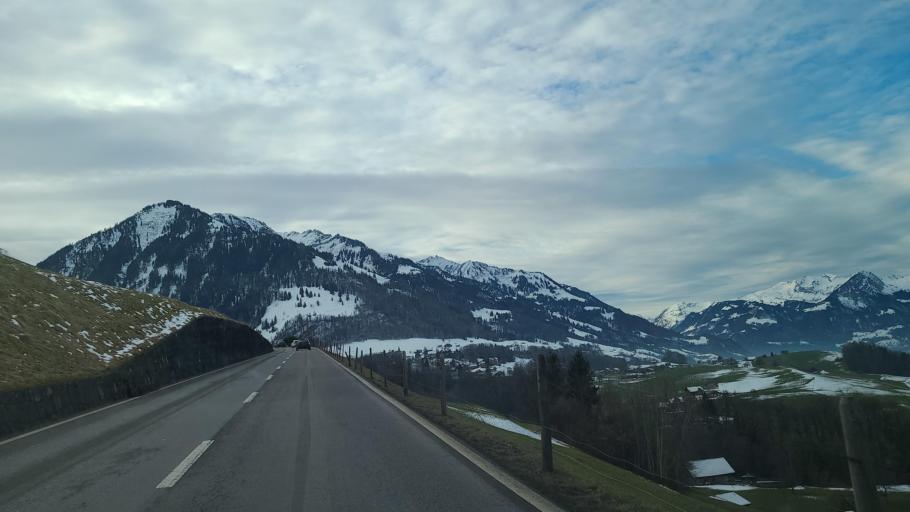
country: CH
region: Obwalden
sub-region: Obwalden
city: Kerns
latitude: 46.8854
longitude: 8.2778
